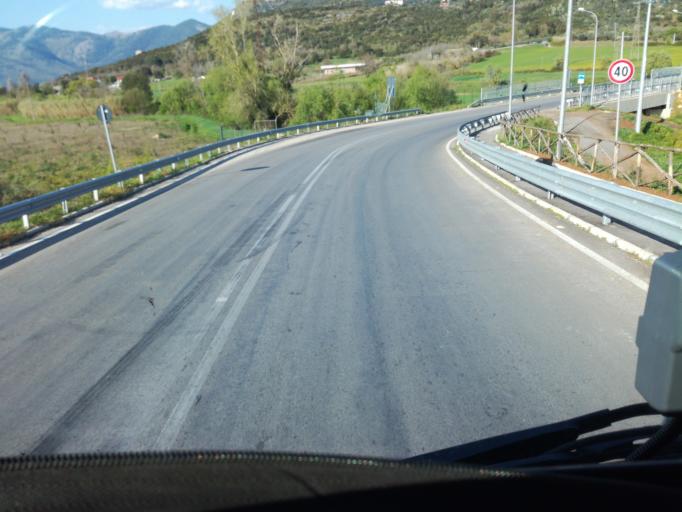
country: IT
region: Latium
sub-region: Provincia di Latina
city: Priverno
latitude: 41.4589
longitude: 13.1987
